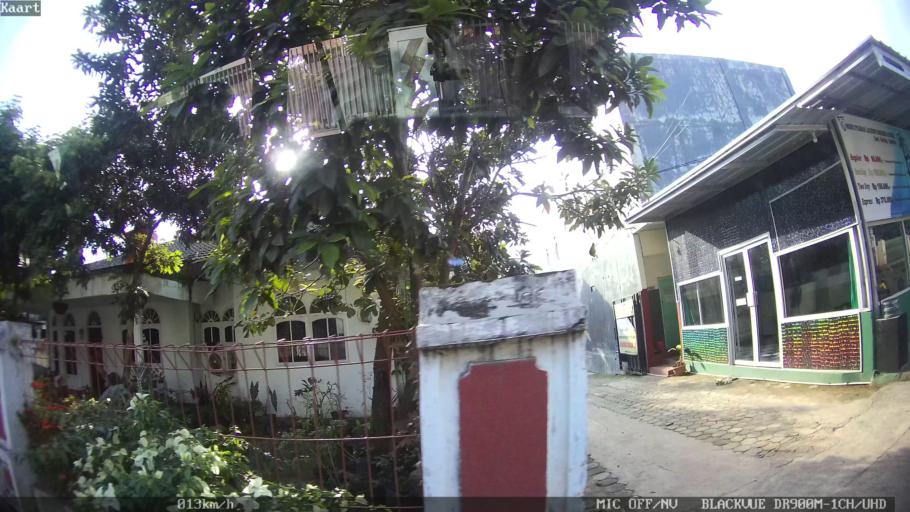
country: ID
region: Lampung
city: Kedaton
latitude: -5.3763
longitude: 105.2416
